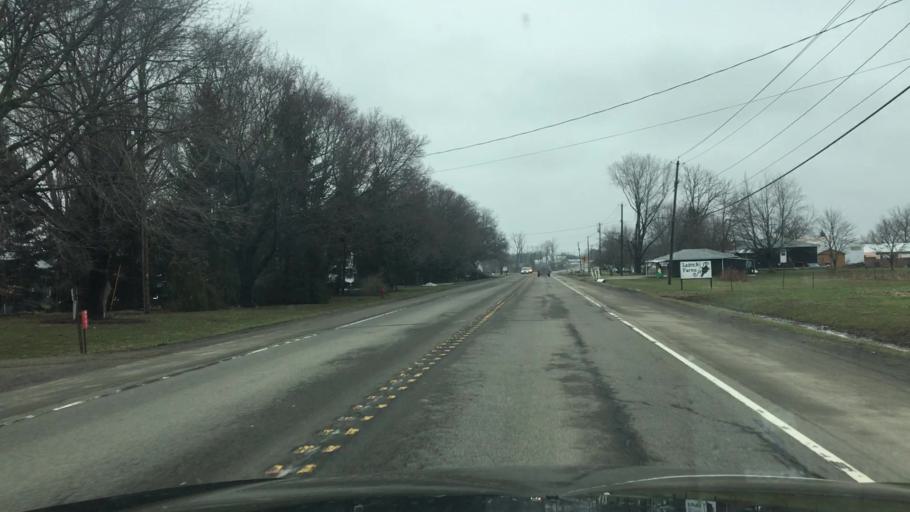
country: US
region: New York
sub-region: Chautauqua County
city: Fredonia
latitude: 42.4270
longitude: -79.3064
